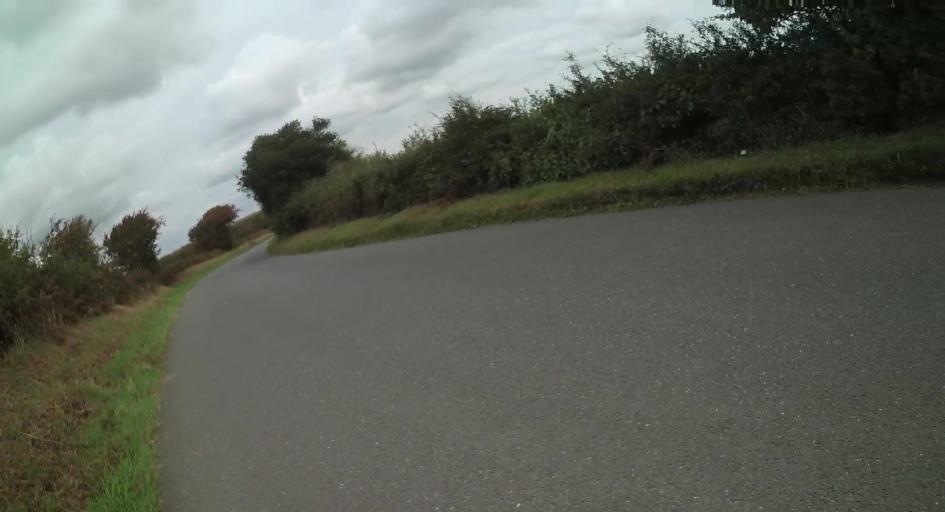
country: GB
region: England
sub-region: Isle of Wight
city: Newport
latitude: 50.6458
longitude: -1.2738
